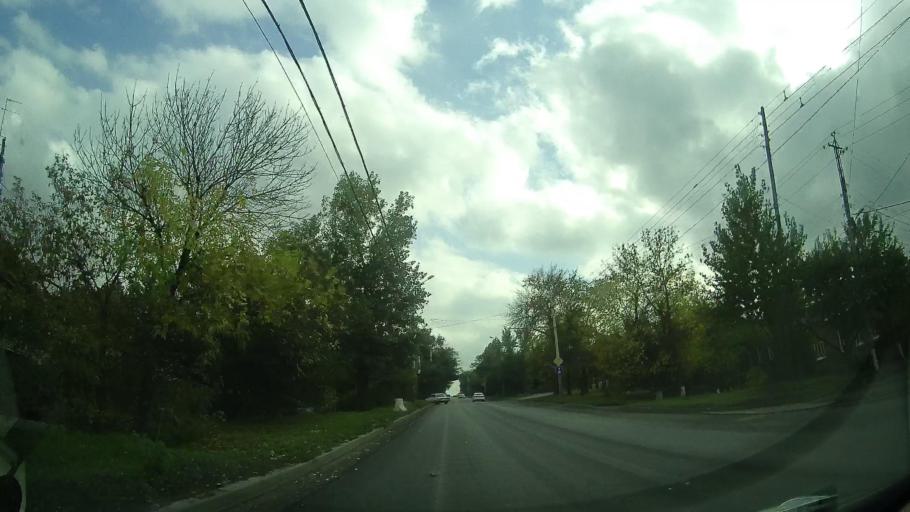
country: RU
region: Rostov
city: Severnyy
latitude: 47.2577
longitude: 39.6910
